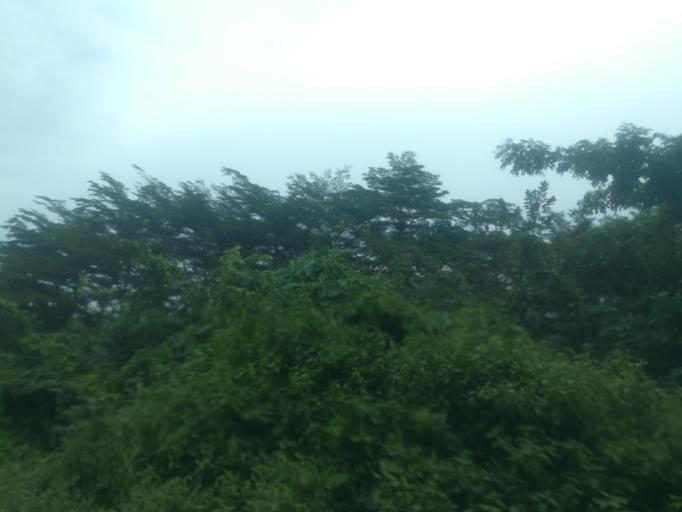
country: NG
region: Oyo
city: Ibadan
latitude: 7.3376
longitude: 3.8960
